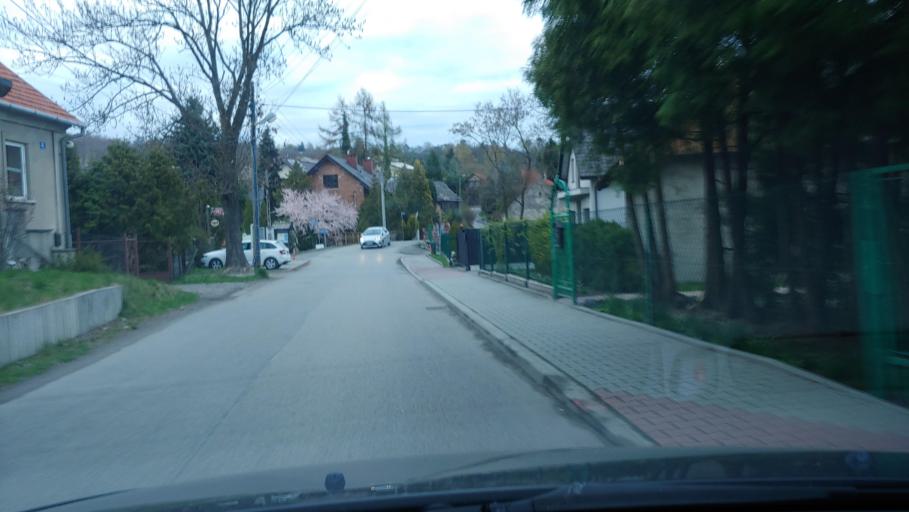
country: PL
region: Lesser Poland Voivodeship
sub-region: Powiat krakowski
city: Bolechowice
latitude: 50.1498
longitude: 19.7612
